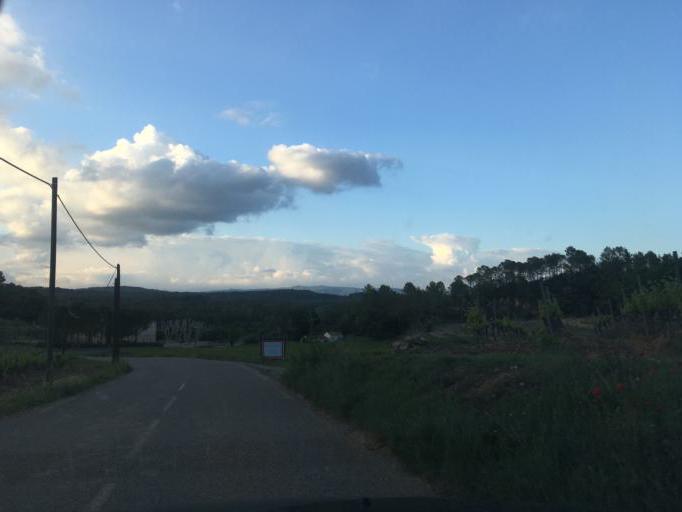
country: FR
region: Provence-Alpes-Cote d'Azur
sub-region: Departement du Var
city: Carces
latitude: 43.4900
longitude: 6.2146
